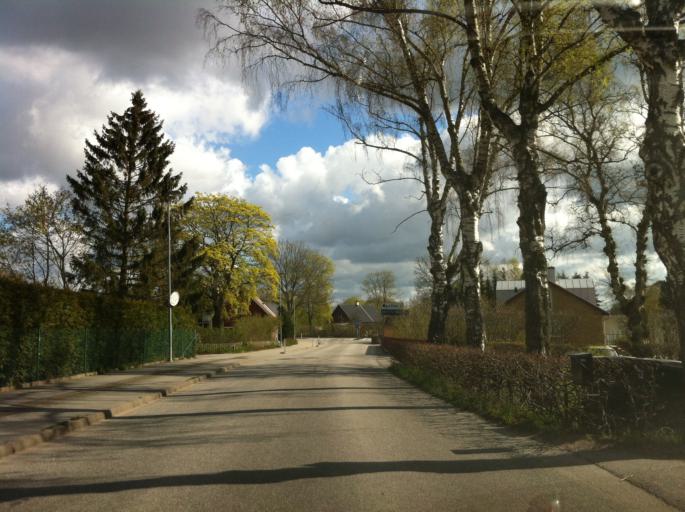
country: SE
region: Skane
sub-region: Hoors Kommun
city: Satofta
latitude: 55.9044
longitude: 13.5450
